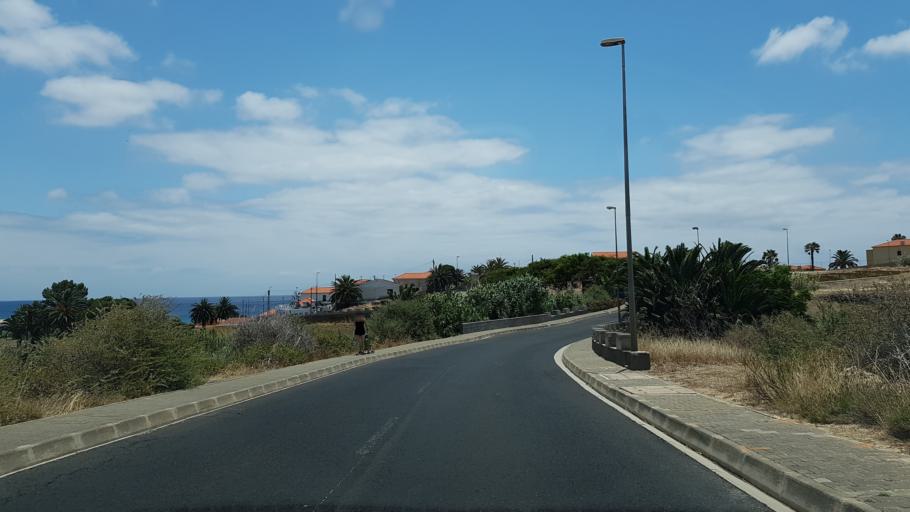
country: PT
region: Madeira
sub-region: Porto Santo
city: Vila de Porto Santo
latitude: 33.0586
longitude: -16.3416
